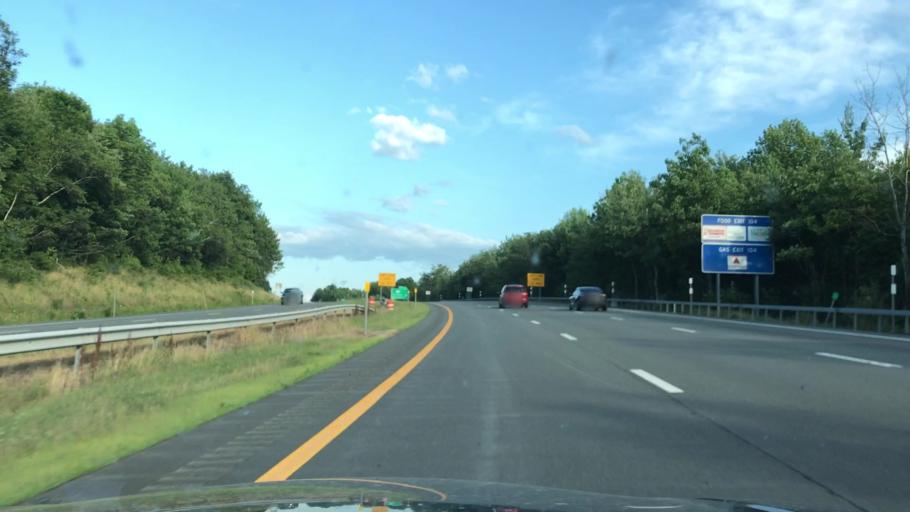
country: US
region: New York
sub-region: Sullivan County
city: Monticello
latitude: 41.6710
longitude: -74.7113
